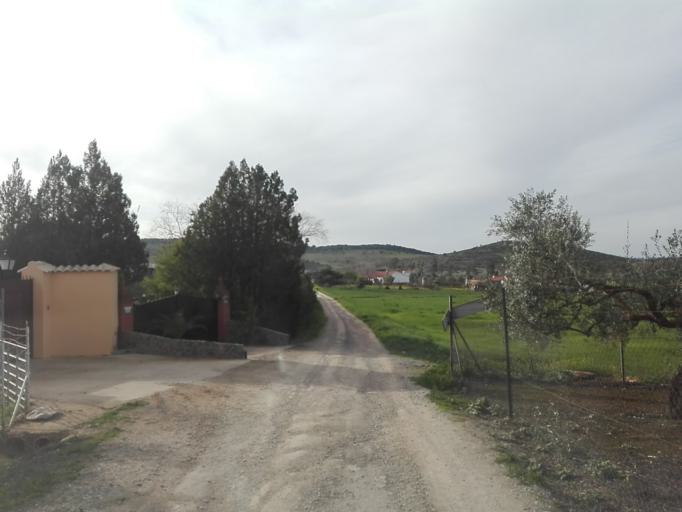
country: ES
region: Extremadura
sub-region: Provincia de Badajoz
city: Llerena
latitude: 38.2235
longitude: -6.0332
